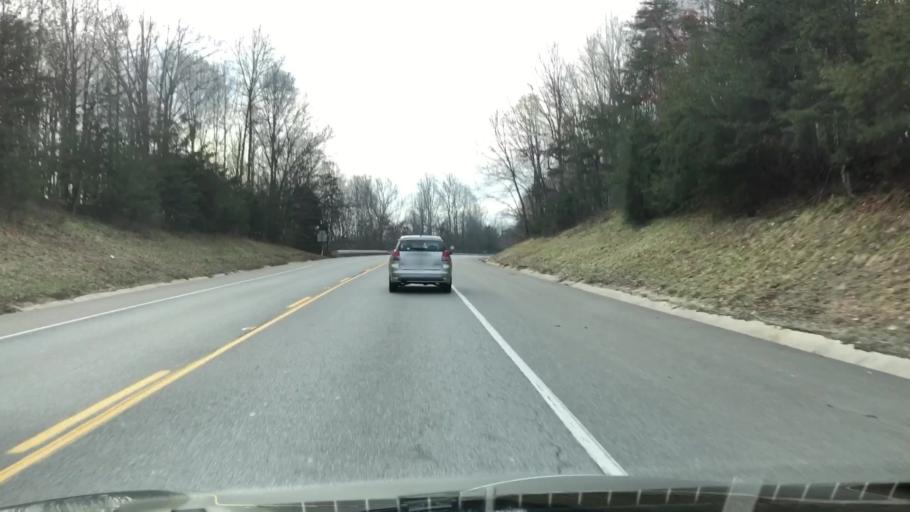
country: US
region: Virginia
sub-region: City of Lynchburg
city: West Lynchburg
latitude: 37.4234
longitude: -79.2321
